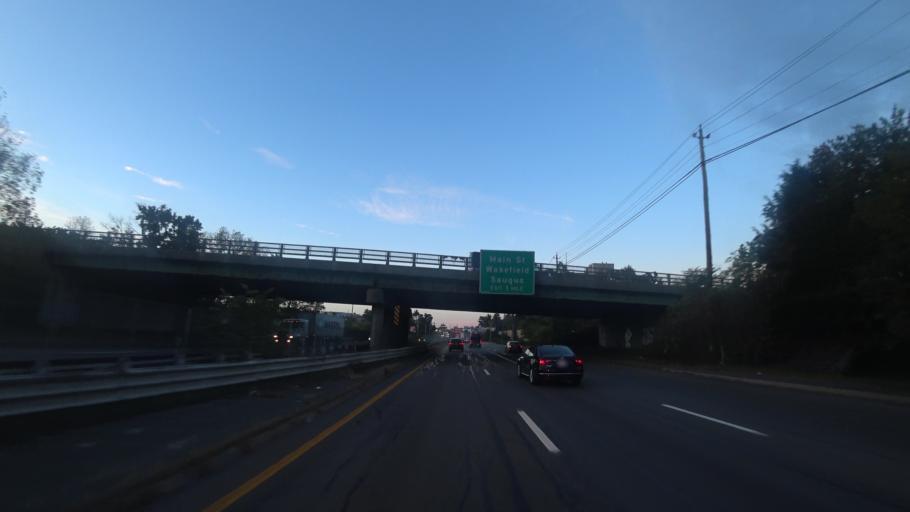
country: US
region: Massachusetts
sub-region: Essex County
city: Saugus
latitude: 42.4812
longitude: -71.0210
